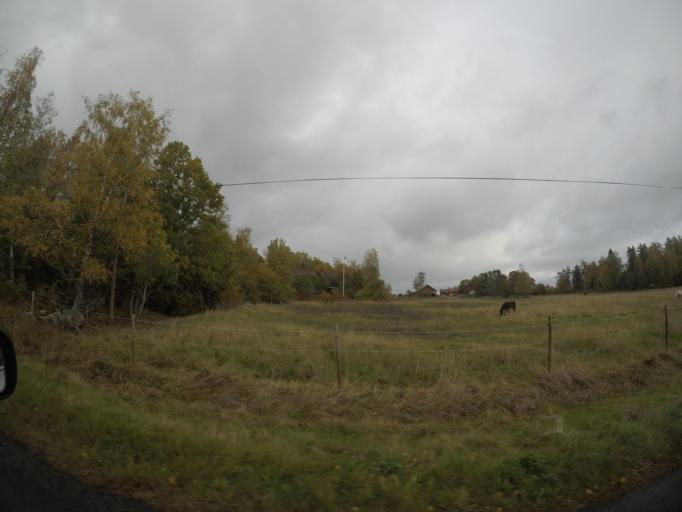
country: SE
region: Soedermanland
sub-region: Eskilstuna Kommun
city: Kvicksund
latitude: 59.3267
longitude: 16.3006
